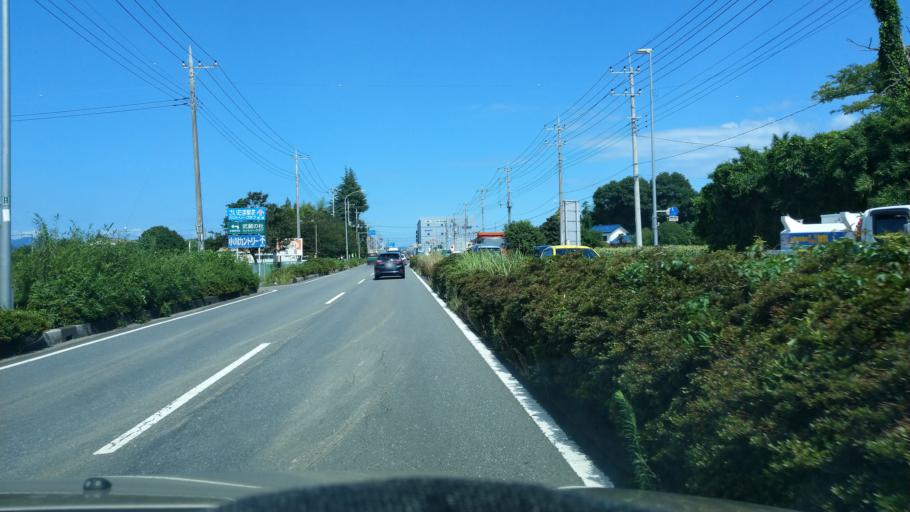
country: JP
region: Saitama
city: Sakado
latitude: 36.0323
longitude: 139.3687
